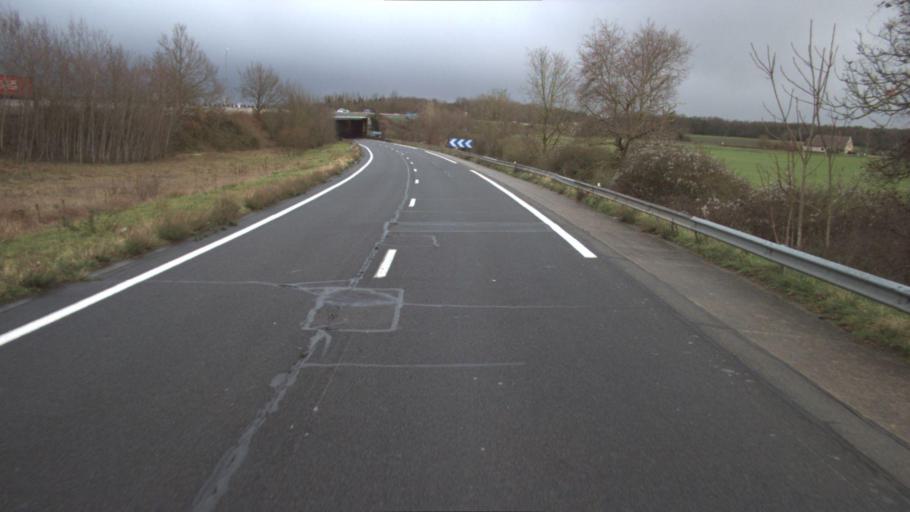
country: FR
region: Ile-de-France
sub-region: Departement de l'Essonne
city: Soisy-sur-Ecole
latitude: 48.4766
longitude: 2.5154
